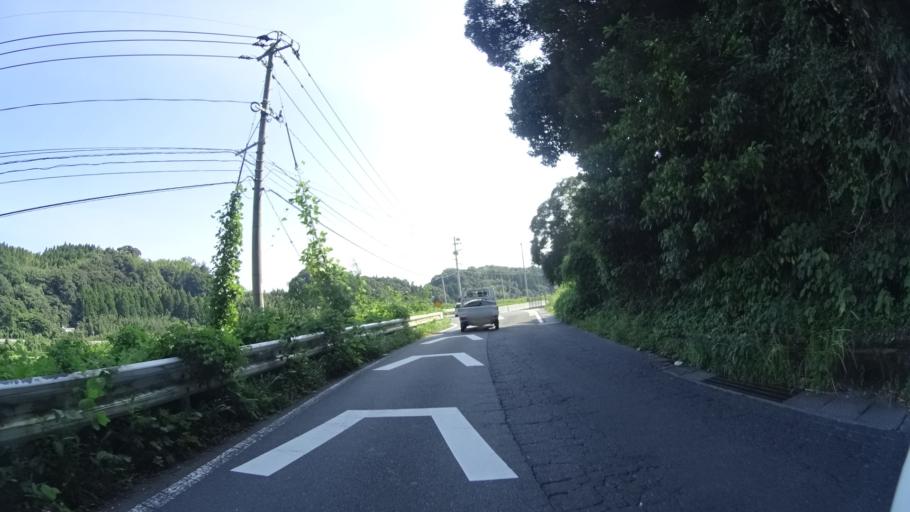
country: JP
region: Kagoshima
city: Kagoshima-shi
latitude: 31.6668
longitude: 130.5584
